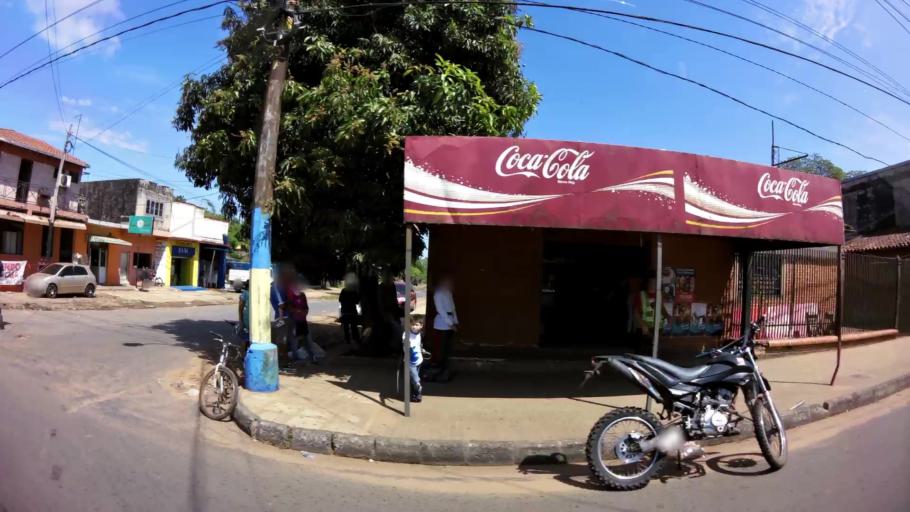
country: PY
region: Central
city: San Lorenzo
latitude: -25.2998
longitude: -57.5035
